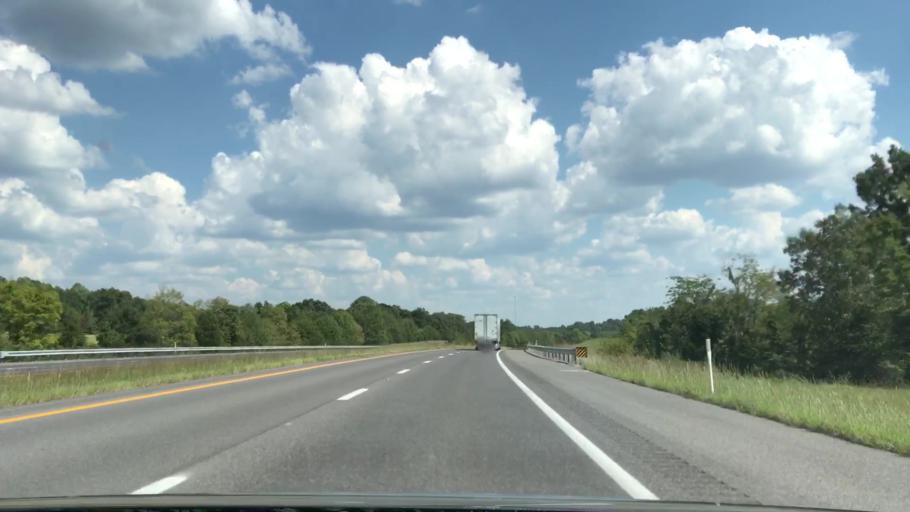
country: US
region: Kentucky
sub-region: Caldwell County
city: Princeton
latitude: 37.1102
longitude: -87.9682
